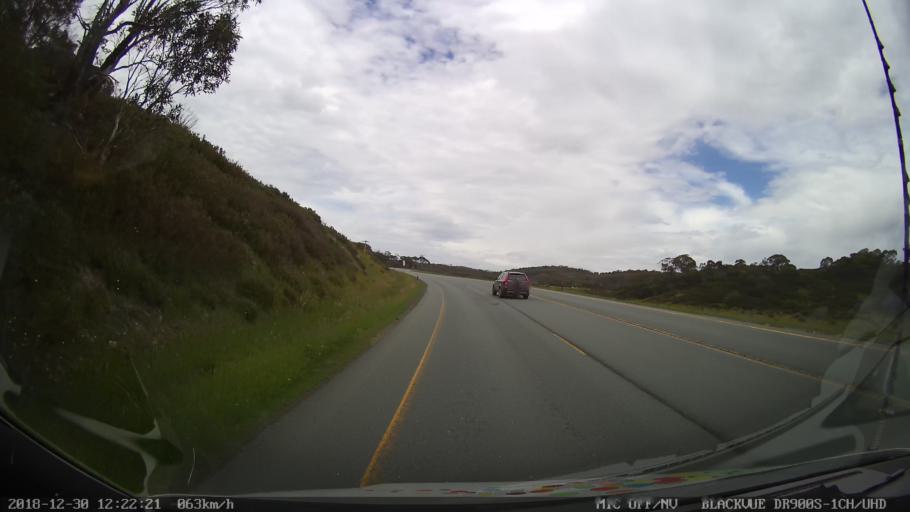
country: AU
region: New South Wales
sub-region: Snowy River
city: Jindabyne
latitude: -36.3584
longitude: 148.5108
